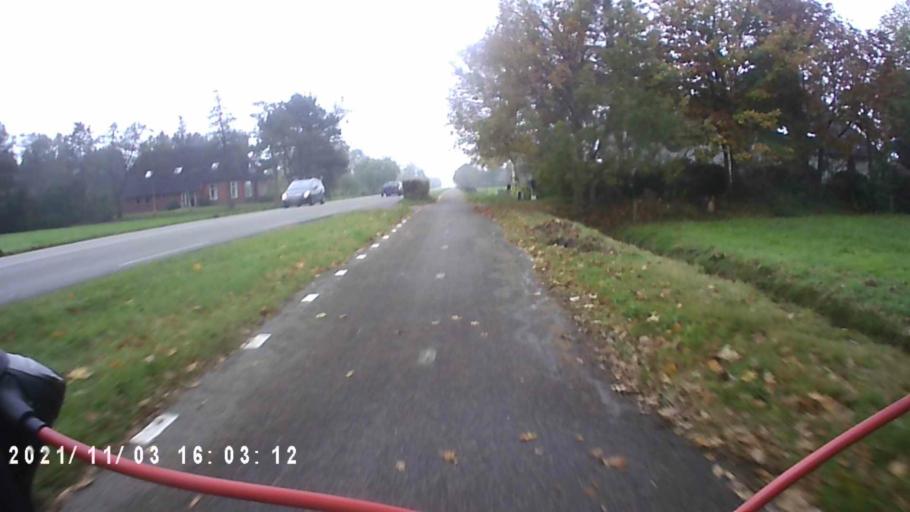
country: NL
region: Groningen
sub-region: Gemeente Leek
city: Leek
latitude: 53.0397
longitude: 6.3307
